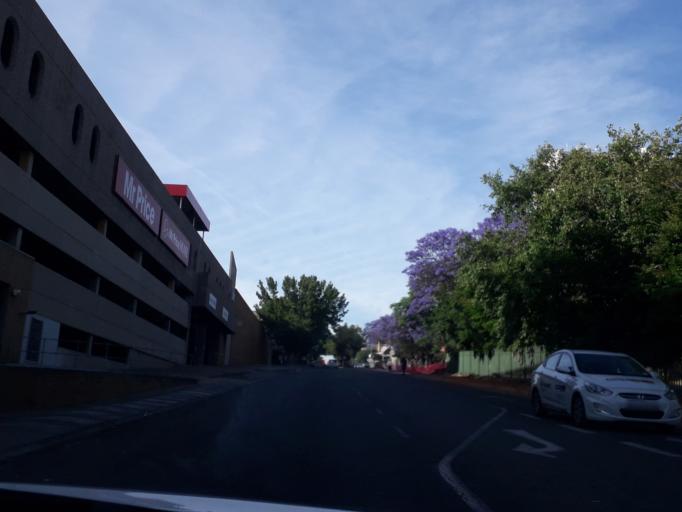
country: ZA
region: Gauteng
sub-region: City of Johannesburg Metropolitan Municipality
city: Johannesburg
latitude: -26.0911
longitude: 28.0027
